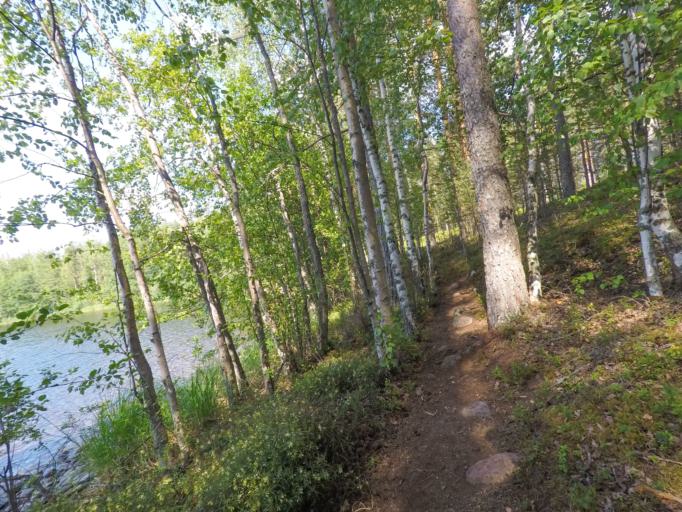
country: FI
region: Southern Savonia
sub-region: Mikkeli
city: Puumala
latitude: 61.4928
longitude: 28.1672
